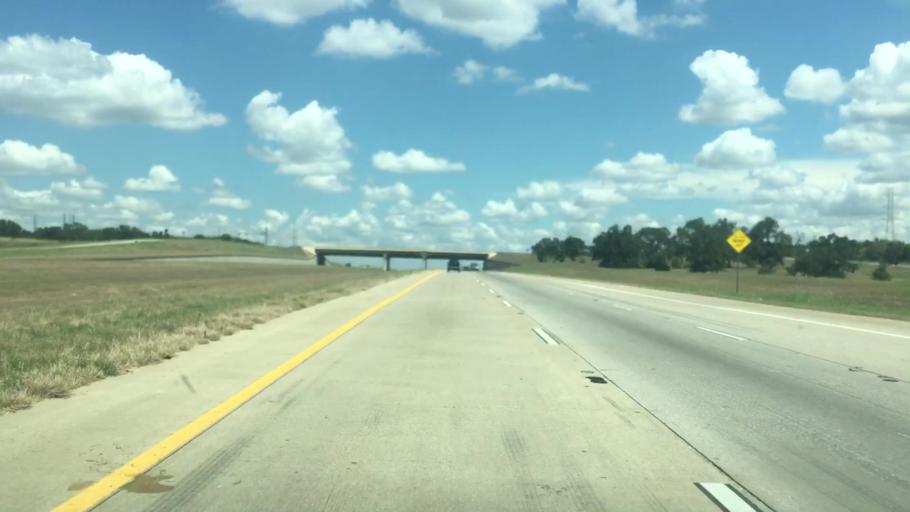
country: US
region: Texas
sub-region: Travis County
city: Hornsby Bend
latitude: 30.2847
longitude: -97.5779
